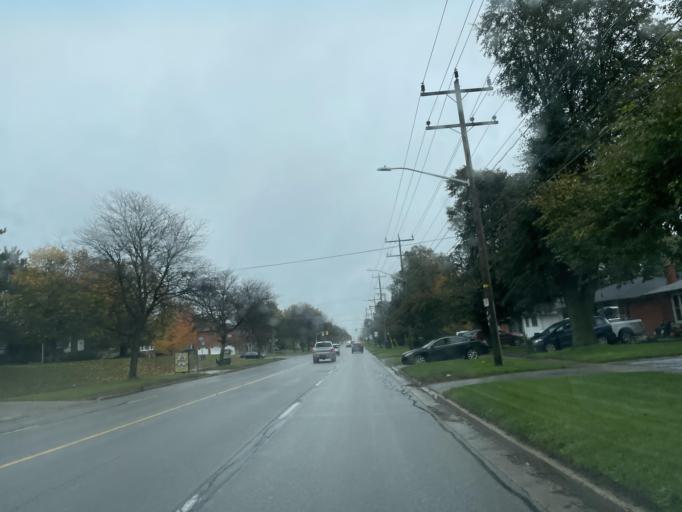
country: CA
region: Ontario
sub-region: Wellington County
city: Guelph
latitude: 43.5756
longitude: -80.2570
